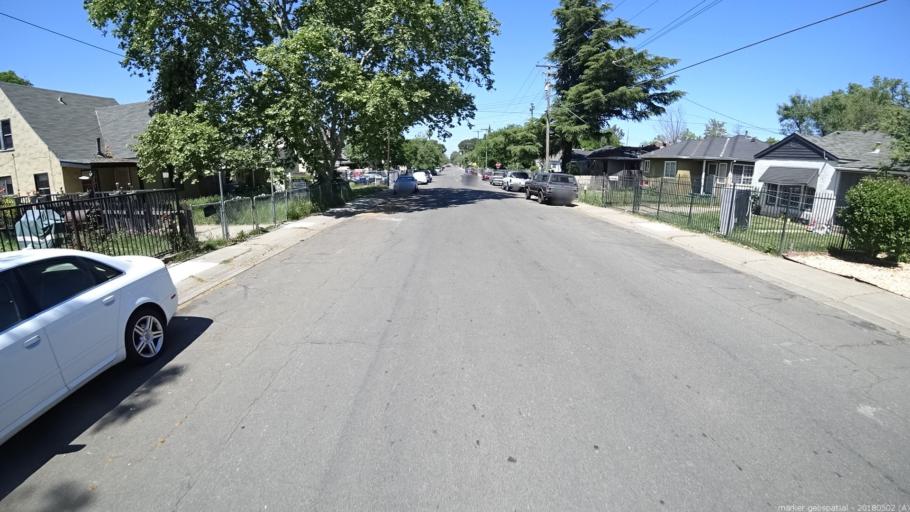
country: US
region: California
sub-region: Sacramento County
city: Sacramento
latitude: 38.6195
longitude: -121.4416
